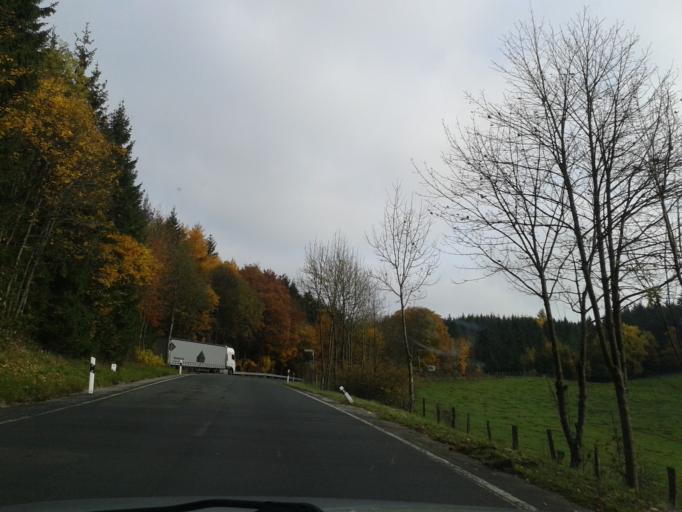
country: DE
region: North Rhine-Westphalia
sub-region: Regierungsbezirk Arnsberg
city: Bad Laasphe
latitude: 50.8661
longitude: 8.3652
